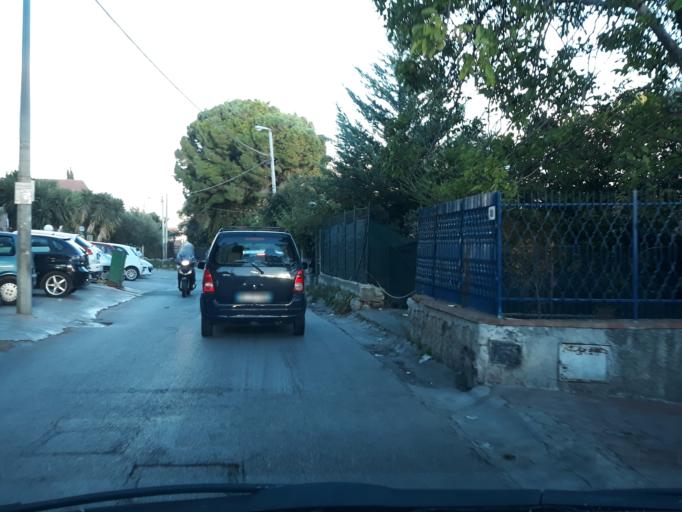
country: IT
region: Sicily
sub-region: Palermo
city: Monreale
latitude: 38.0747
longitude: 13.3050
